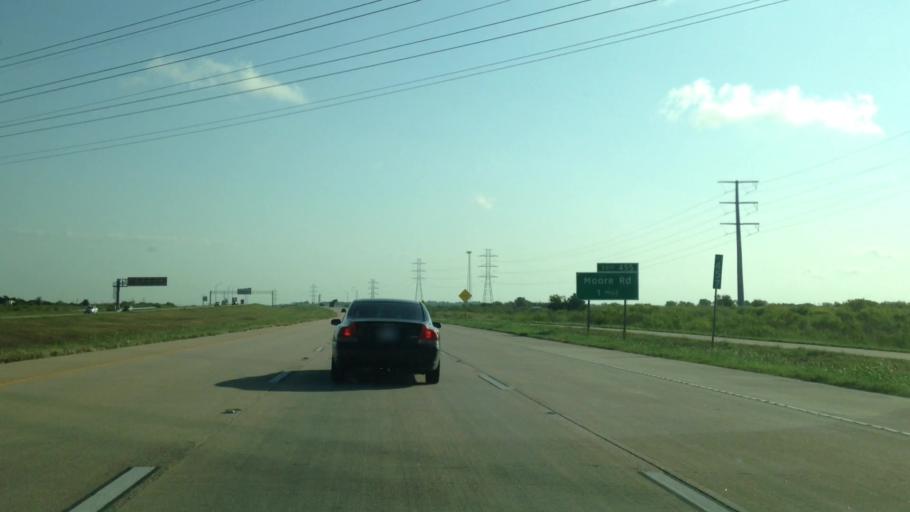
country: US
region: Texas
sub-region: Travis County
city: Onion Creek
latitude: 30.0951
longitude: -97.6758
